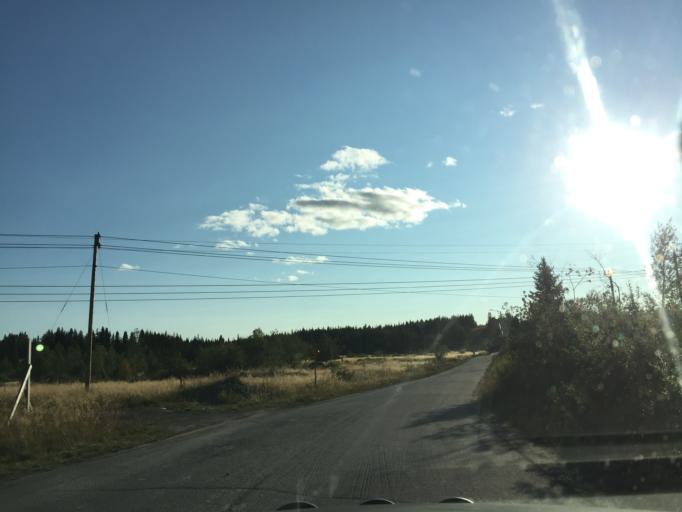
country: SE
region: Norrbotten
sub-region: Gallivare Kommun
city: Malmberget
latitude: 67.6451
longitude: 21.0406
